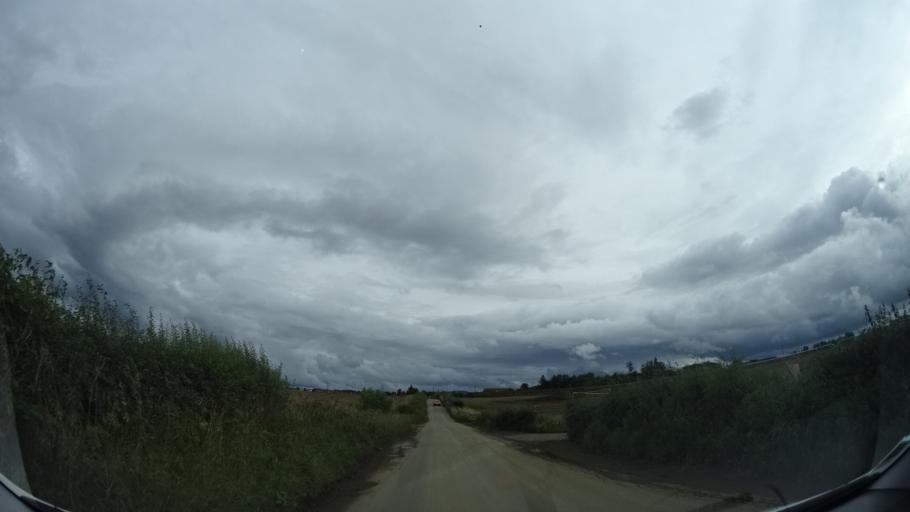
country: GB
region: Scotland
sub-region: West Lothian
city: Kirknewton
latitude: 55.9033
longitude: -3.4345
